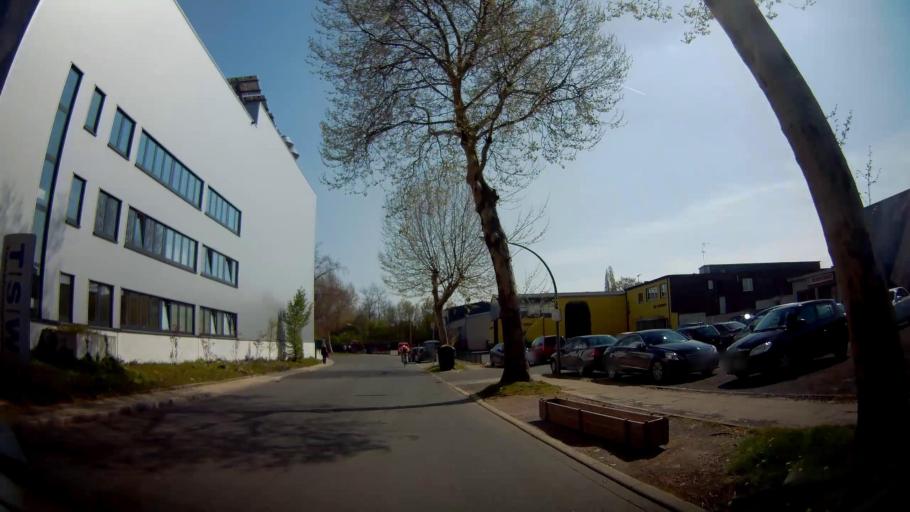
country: DE
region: North Rhine-Westphalia
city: Bochum-Hordel
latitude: 51.4836
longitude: 7.1589
